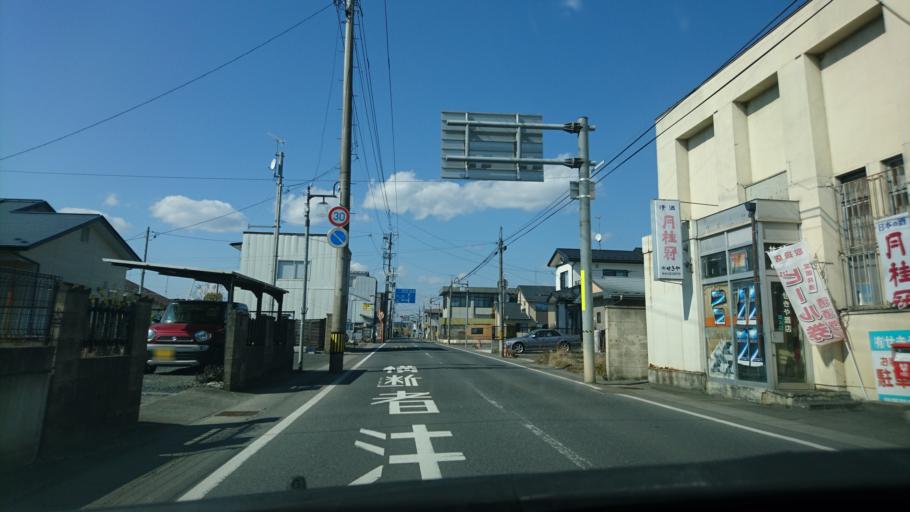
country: JP
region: Miyagi
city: Wakuya
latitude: 38.7064
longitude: 141.2883
